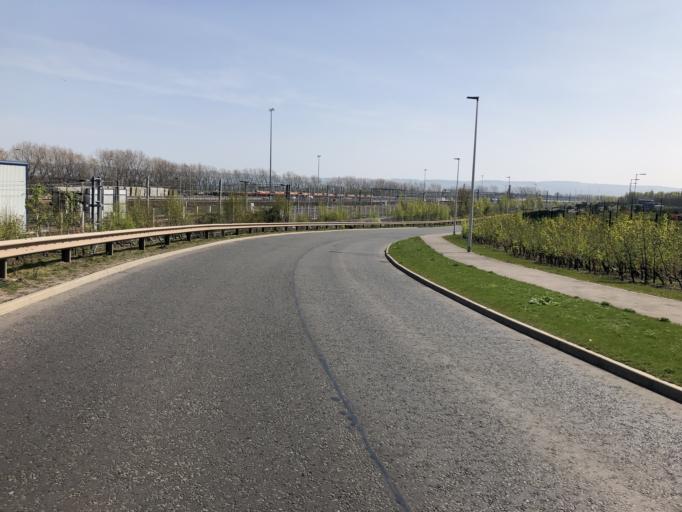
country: GB
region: Scotland
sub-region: Midlothian
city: Dalkeith
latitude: 55.9271
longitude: -3.0862
